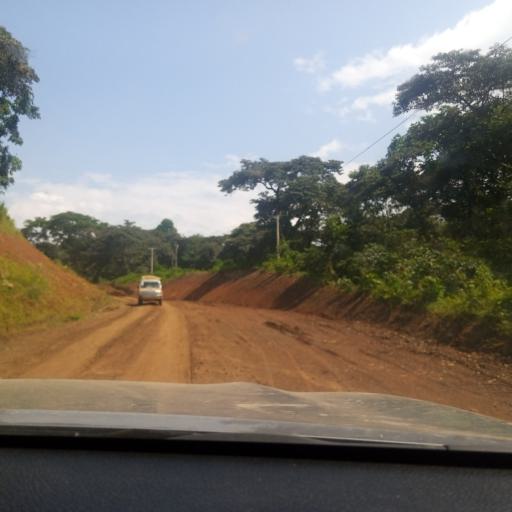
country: ET
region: Southern Nations, Nationalities, and People's Region
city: Tippi
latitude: 7.0714
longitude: 35.4319
